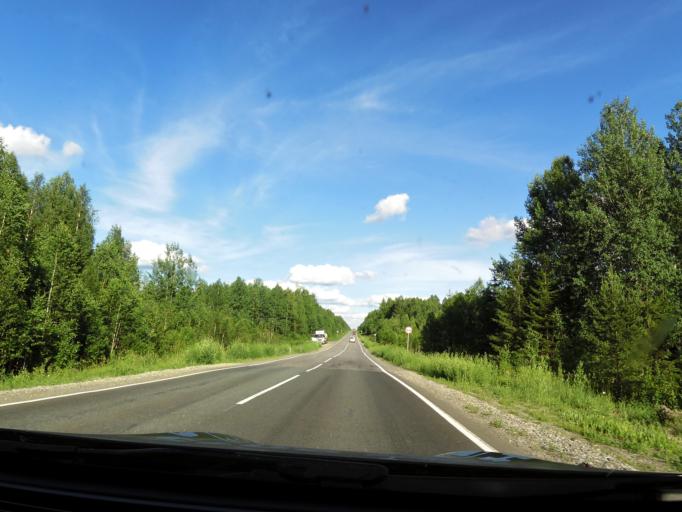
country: RU
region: Kirov
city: Chernaya Kholunitsa
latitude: 58.7731
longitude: 51.9423
